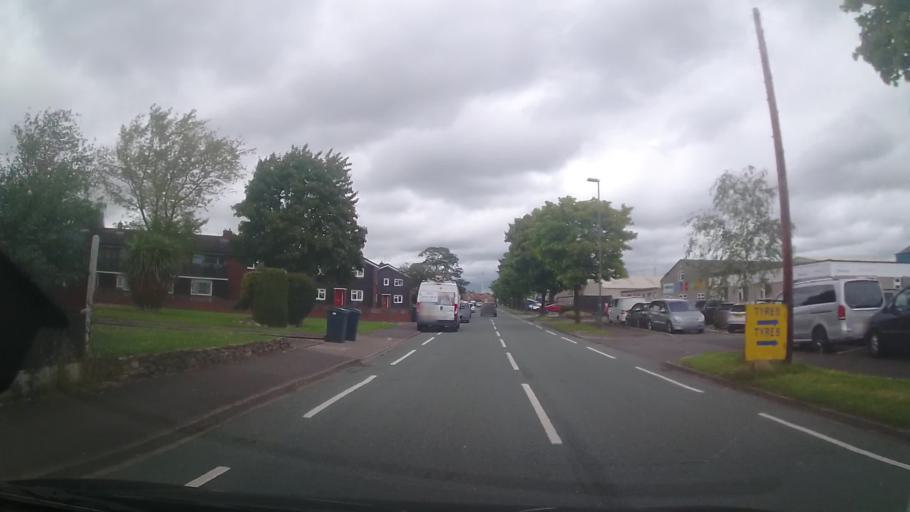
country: GB
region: England
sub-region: Shropshire
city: Shrewsbury
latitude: 52.7346
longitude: -2.7373
